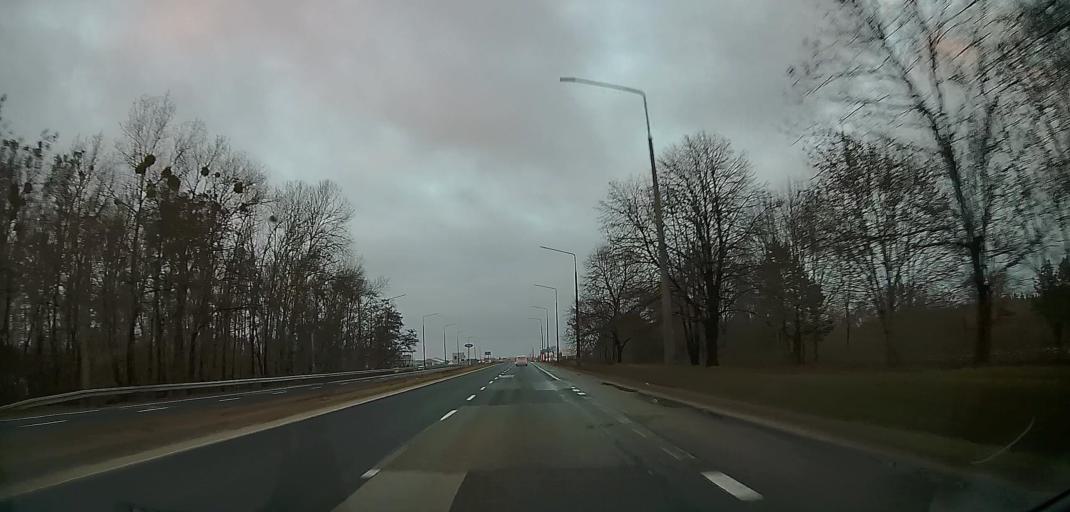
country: PL
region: Masovian Voivodeship
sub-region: Radom
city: Radom
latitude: 51.4567
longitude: 21.1411
